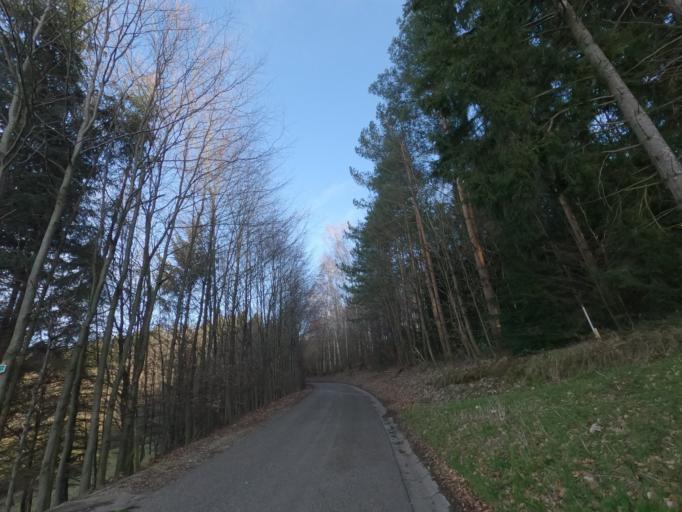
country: DE
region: Baden-Wuerttemberg
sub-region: Regierungsbezirk Stuttgart
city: Donzdorf
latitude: 48.7251
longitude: 9.8004
